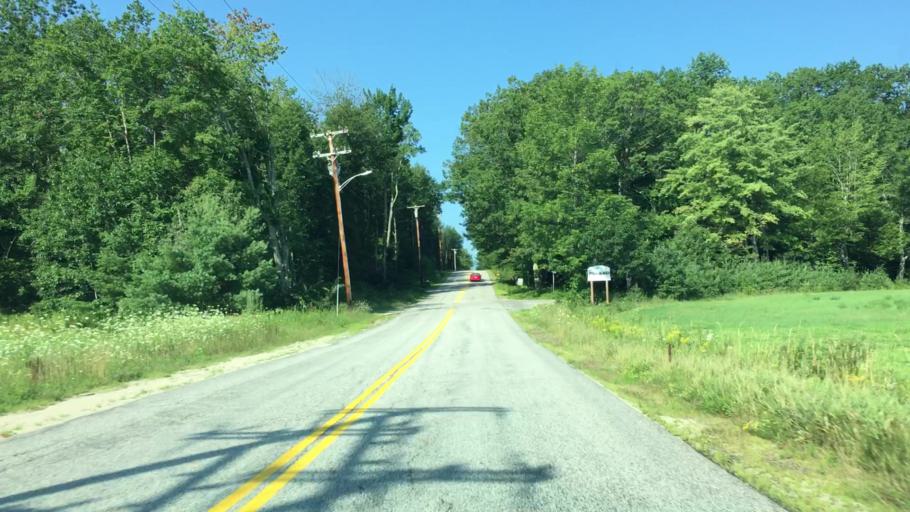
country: US
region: Maine
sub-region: Androscoggin County
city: Minot
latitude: 44.0445
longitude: -70.3085
